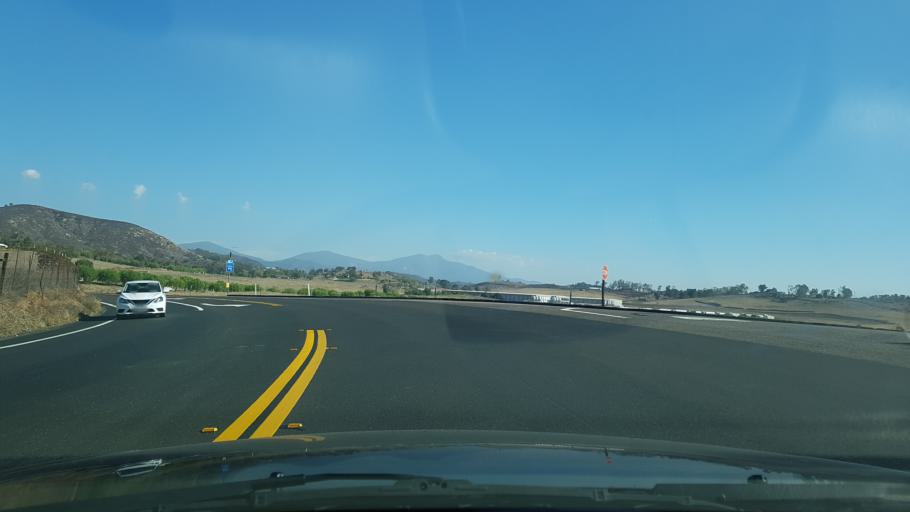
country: US
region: California
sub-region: San Diego County
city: San Diego Country Estates
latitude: 33.0796
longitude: -116.7831
